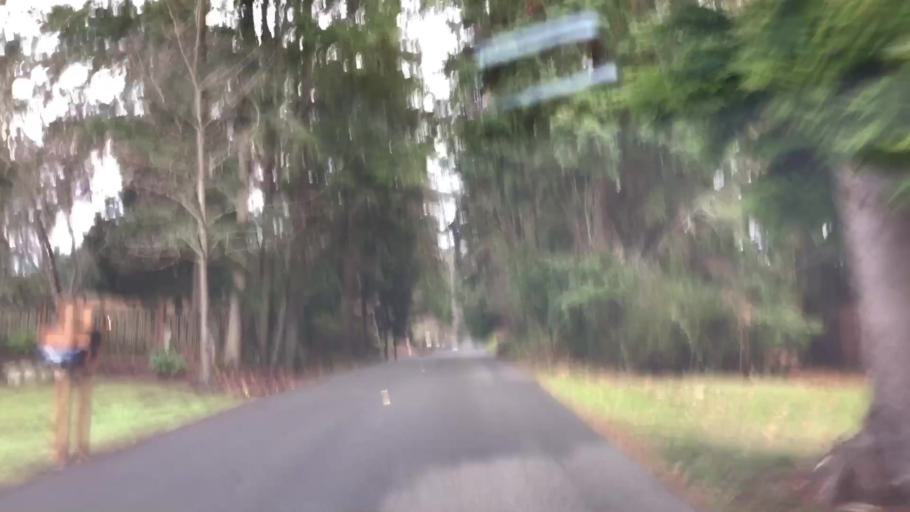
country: US
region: Washington
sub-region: King County
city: Cottage Lake
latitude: 47.7401
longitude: -122.0844
